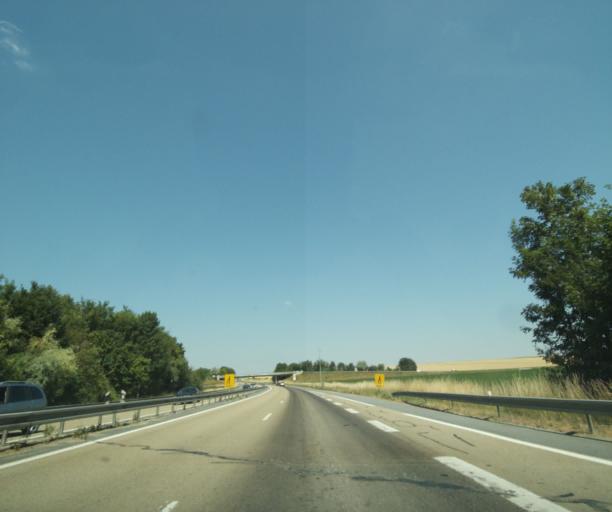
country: FR
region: Champagne-Ardenne
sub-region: Departement de la Marne
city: Sarry
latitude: 48.8664
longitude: 4.4838
